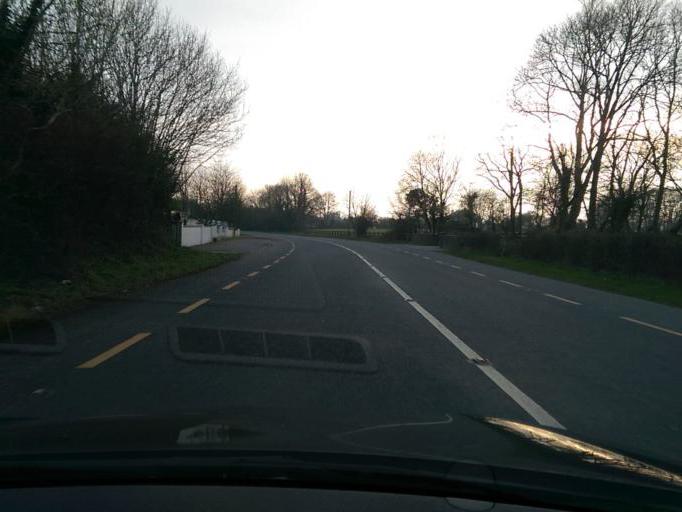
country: IE
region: Leinster
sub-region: An Longfort
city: Ballymahon
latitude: 53.5071
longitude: -7.8328
